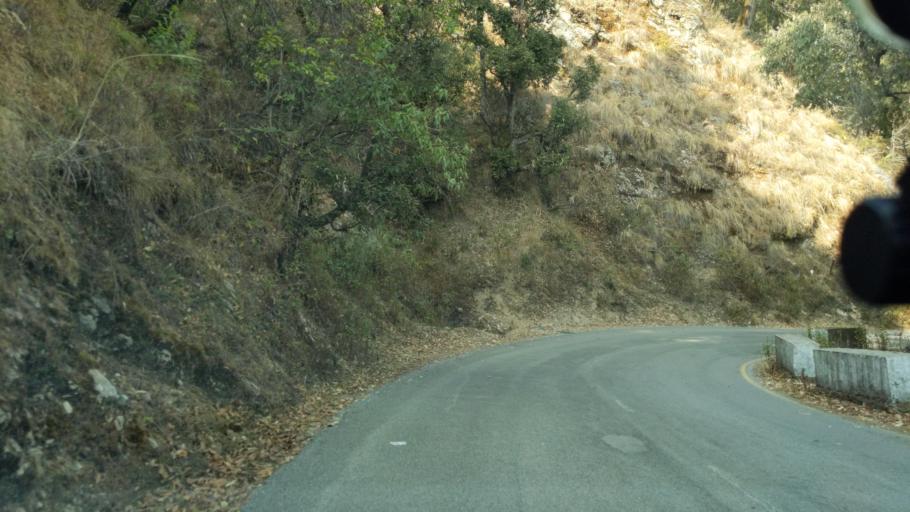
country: IN
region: Uttarakhand
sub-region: Naini Tal
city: Bhowali
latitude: 29.4020
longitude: 79.5347
